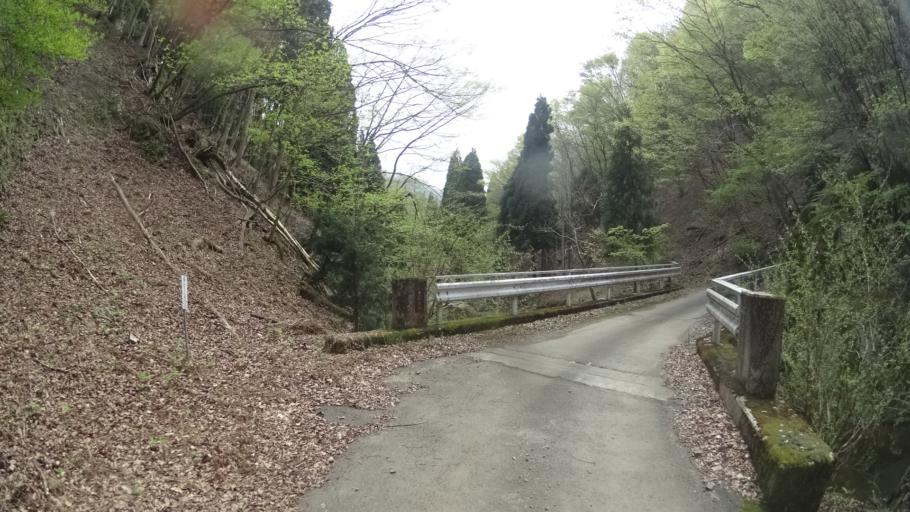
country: JP
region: Kyoto
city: Maizuru
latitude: 35.4058
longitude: 135.5059
